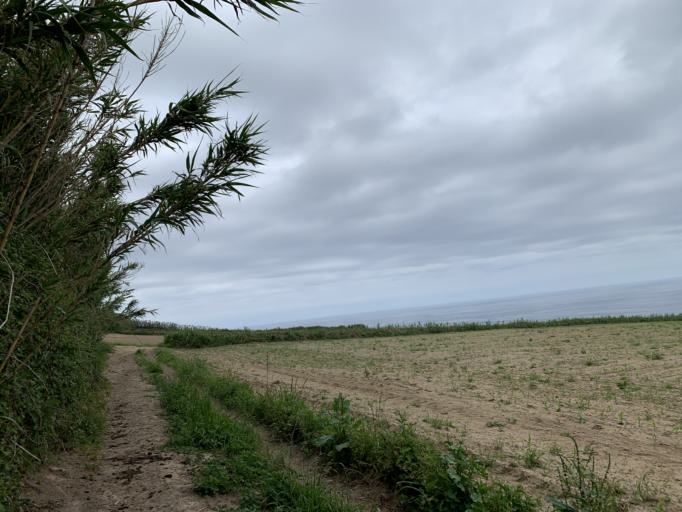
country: PT
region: Azores
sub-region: Ponta Delgada
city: Arrifes
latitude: 37.8517
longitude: -25.8485
